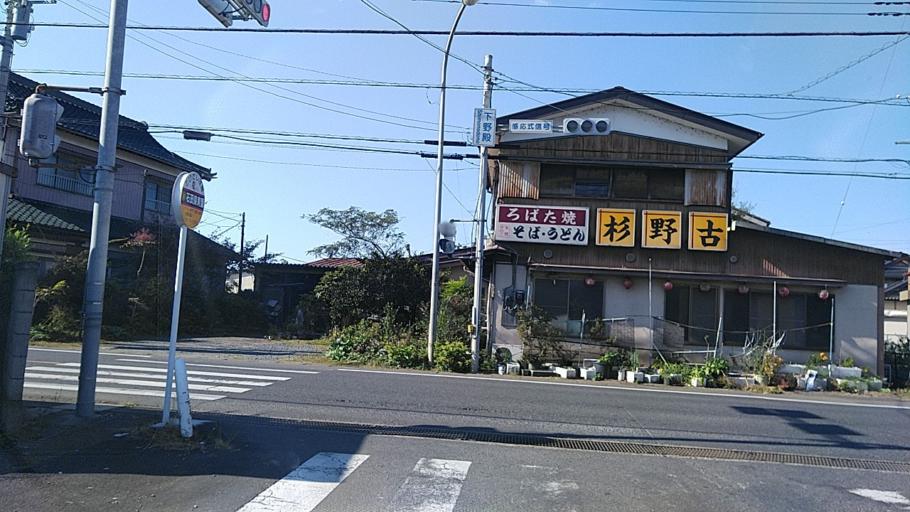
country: JP
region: Ibaraki
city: Shimodate
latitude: 36.2712
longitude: 139.9713
